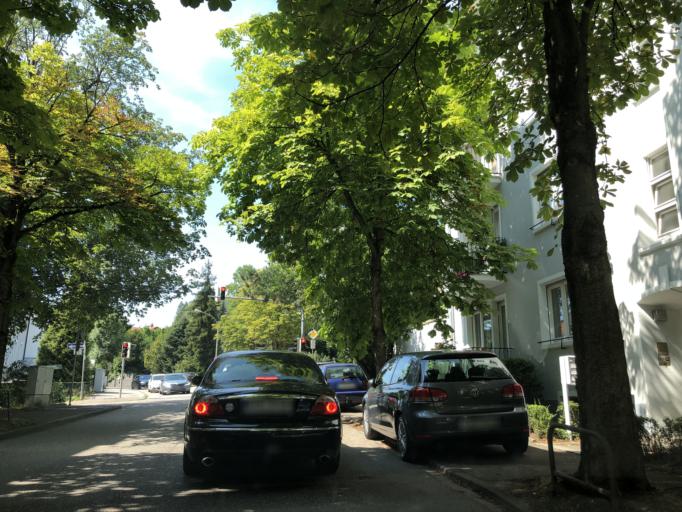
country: DE
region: Baden-Wuerttemberg
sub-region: Karlsruhe Region
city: Baden-Baden
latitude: 48.7499
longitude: 8.2538
